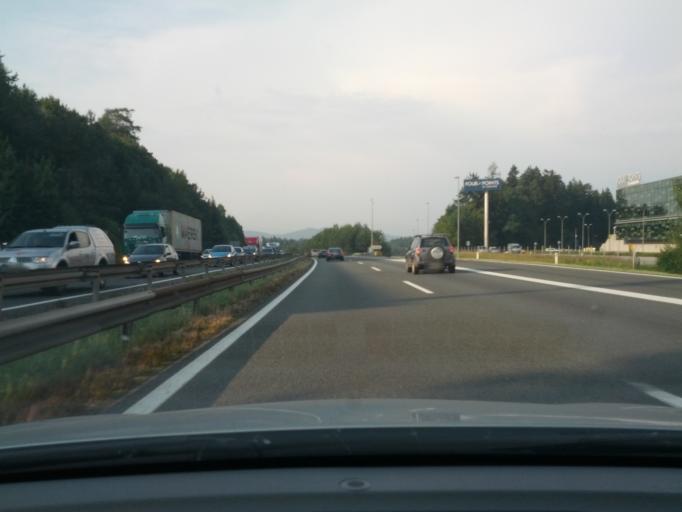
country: SI
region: Brezovica
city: Vnanje Gorice
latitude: 46.0514
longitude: 14.4512
